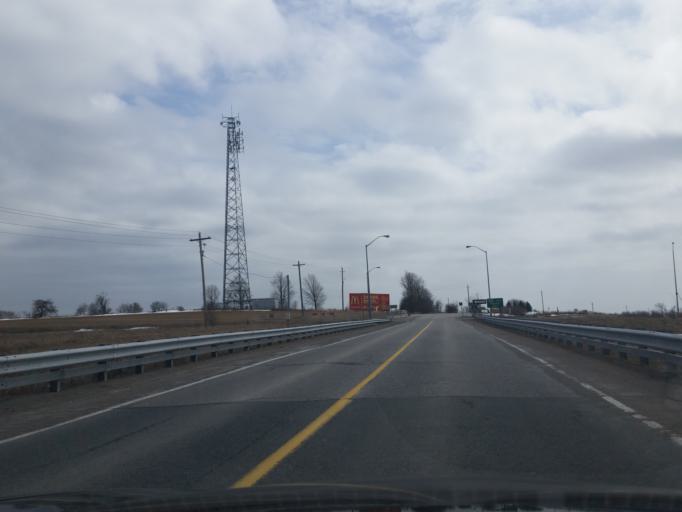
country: CA
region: Ontario
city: Cobourg
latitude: 43.9534
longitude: -78.3875
